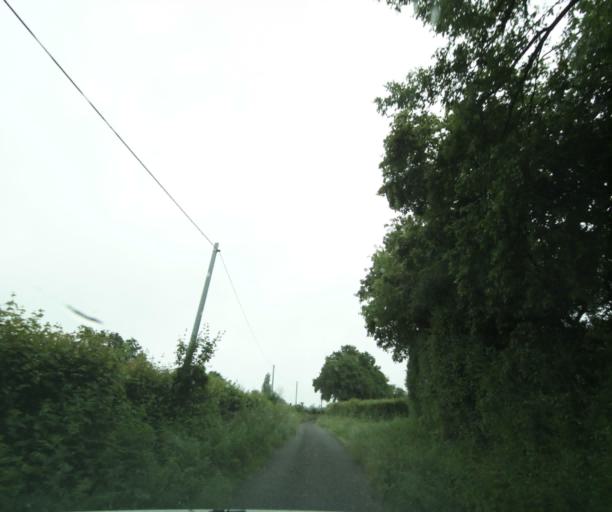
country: FR
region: Bourgogne
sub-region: Departement de Saone-et-Loire
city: La Clayette
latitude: 46.3476
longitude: 4.2140
